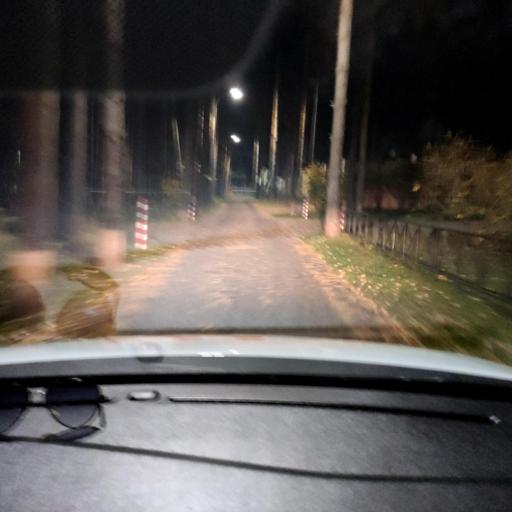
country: RU
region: Tatarstan
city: Verkhniy Uslon
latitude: 55.6222
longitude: 49.0201
